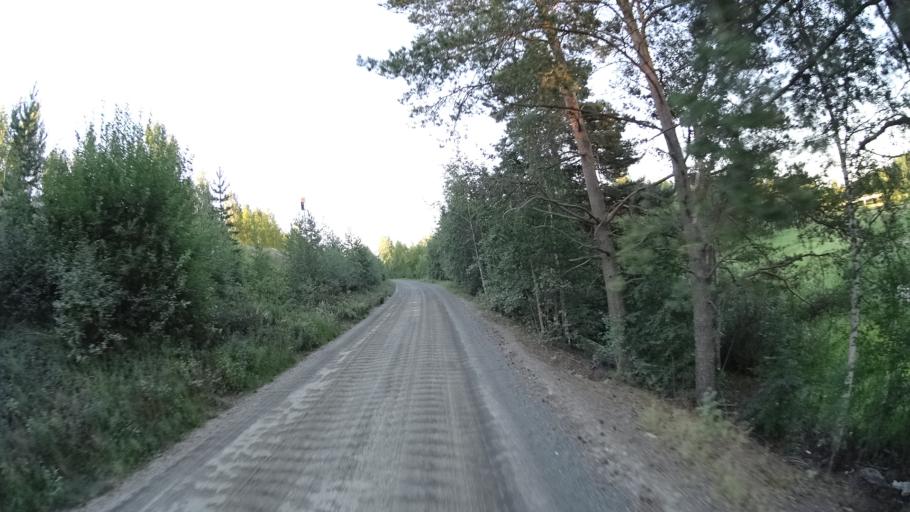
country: FI
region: Central Finland
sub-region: Jyvaeskylae
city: Petaejaevesi
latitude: 62.2556
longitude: 25.1752
